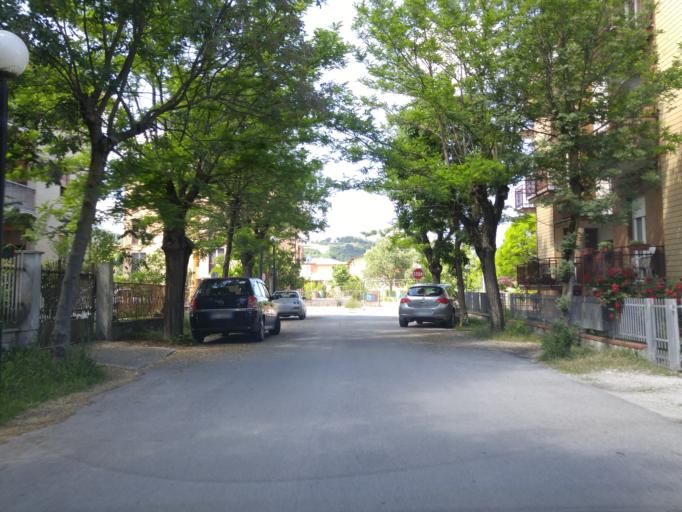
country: IT
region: The Marches
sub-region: Provincia di Pesaro e Urbino
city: Fermignano
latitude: 43.6822
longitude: 12.6462
